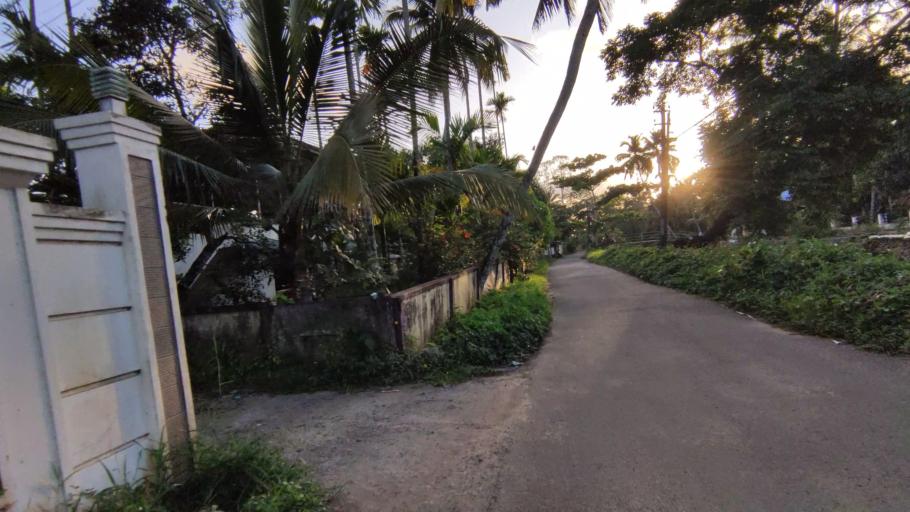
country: IN
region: Kerala
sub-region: Kottayam
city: Kottayam
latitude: 9.5958
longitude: 76.4648
